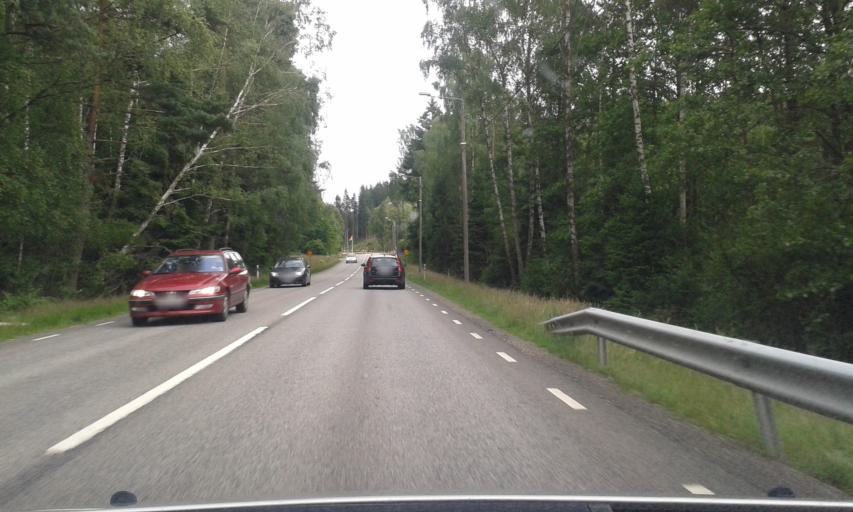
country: SE
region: Halland
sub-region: Varbergs Kommun
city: Tvaaker
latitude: 57.1410
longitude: 12.6968
